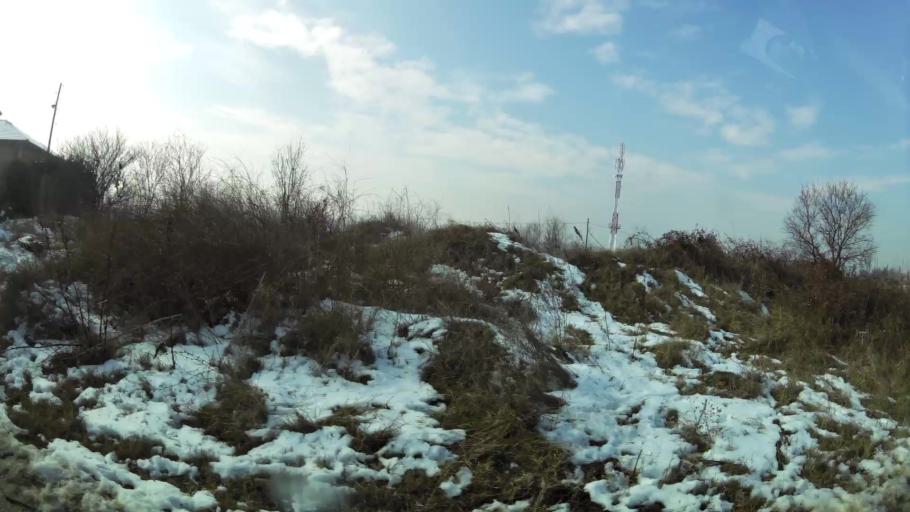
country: MK
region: Suto Orizari
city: Suto Orizare
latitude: 42.0318
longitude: 21.3771
